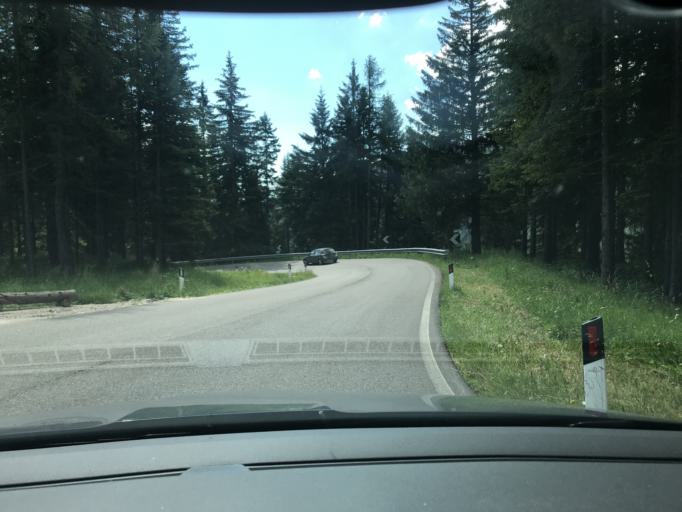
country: IT
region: Veneto
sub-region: Provincia di Belluno
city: Cortina d'Ampezzo
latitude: 46.5200
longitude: 12.0933
